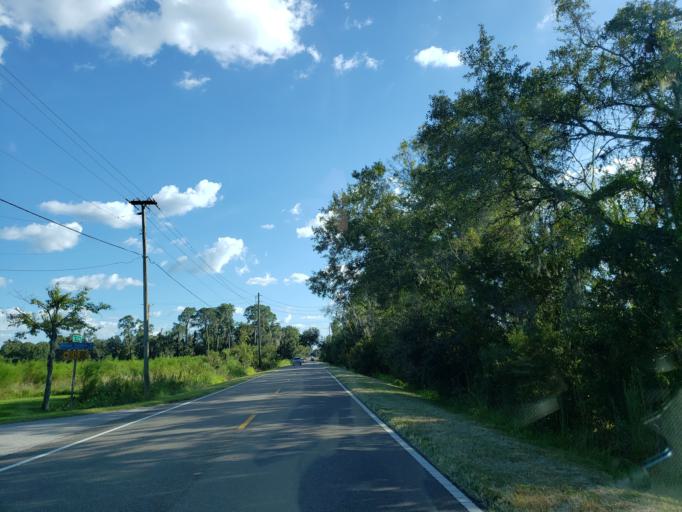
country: US
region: Florida
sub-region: Hillsborough County
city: Valrico
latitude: 27.9623
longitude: -82.2197
